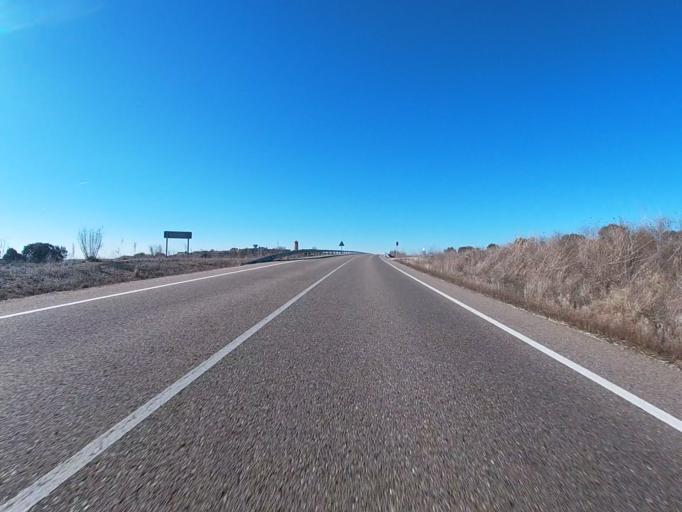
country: ES
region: Castille and Leon
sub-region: Provincia de Salamanca
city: Juzbado
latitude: 41.0783
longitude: -5.8549
